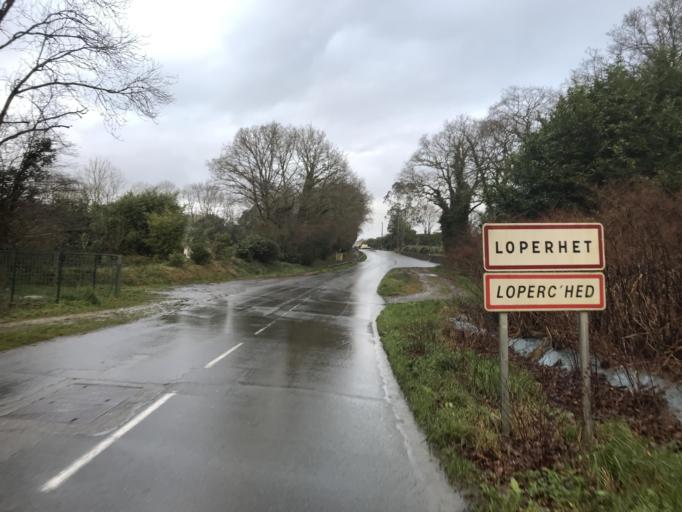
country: FR
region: Brittany
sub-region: Departement du Finistere
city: Loperhet
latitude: 48.3691
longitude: -4.3074
